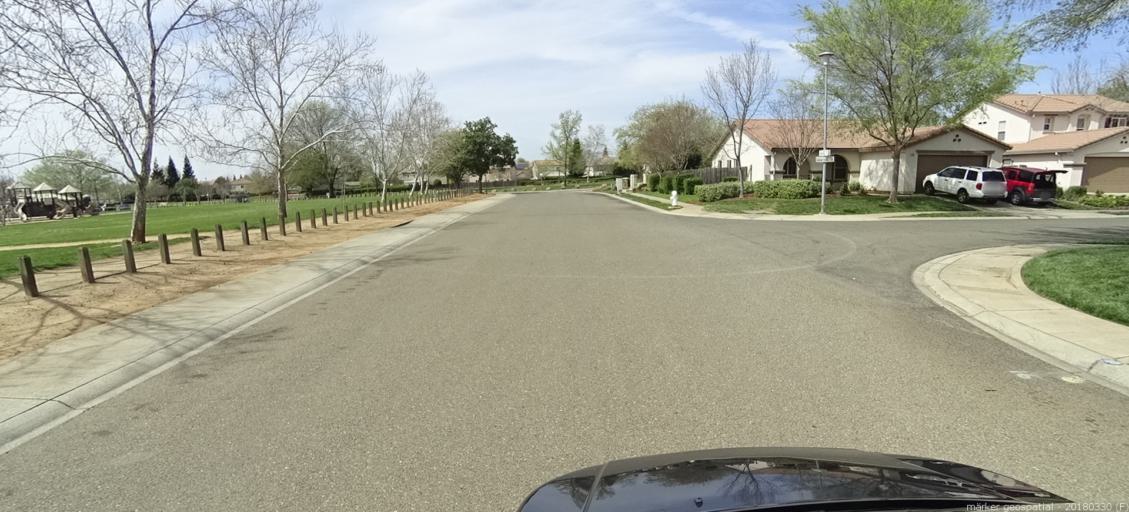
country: US
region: California
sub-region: Sacramento County
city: Rancho Cordova
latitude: 38.5458
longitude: -121.2765
